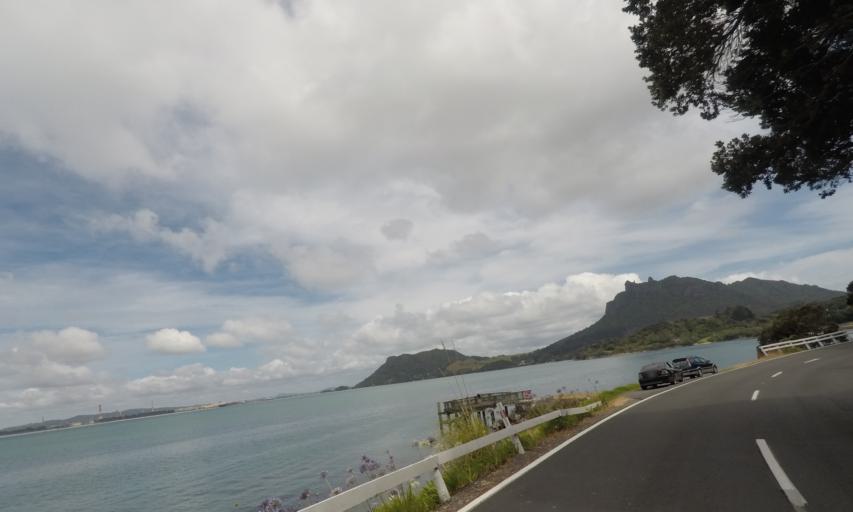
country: NZ
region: Northland
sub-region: Whangarei
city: Ruakaka
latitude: -35.8396
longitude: 174.5338
